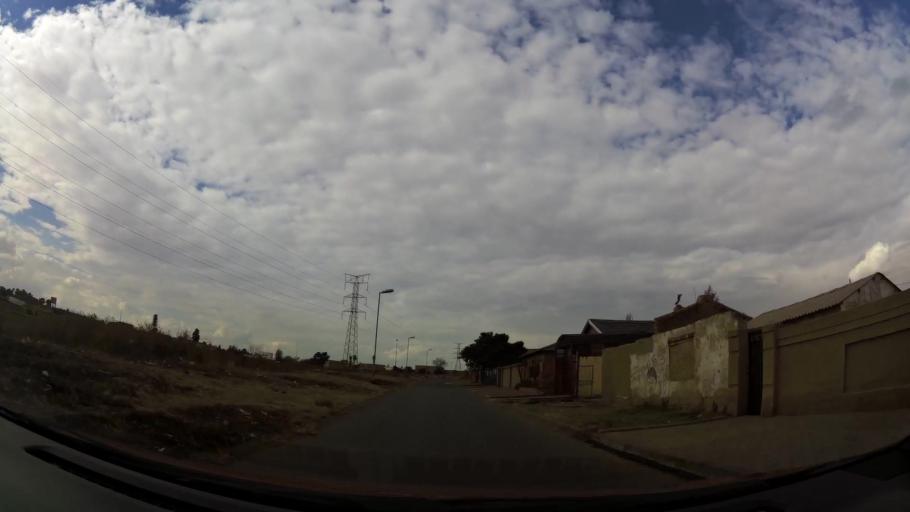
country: ZA
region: Gauteng
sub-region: City of Johannesburg Metropolitan Municipality
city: Soweto
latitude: -26.2417
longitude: 27.8504
